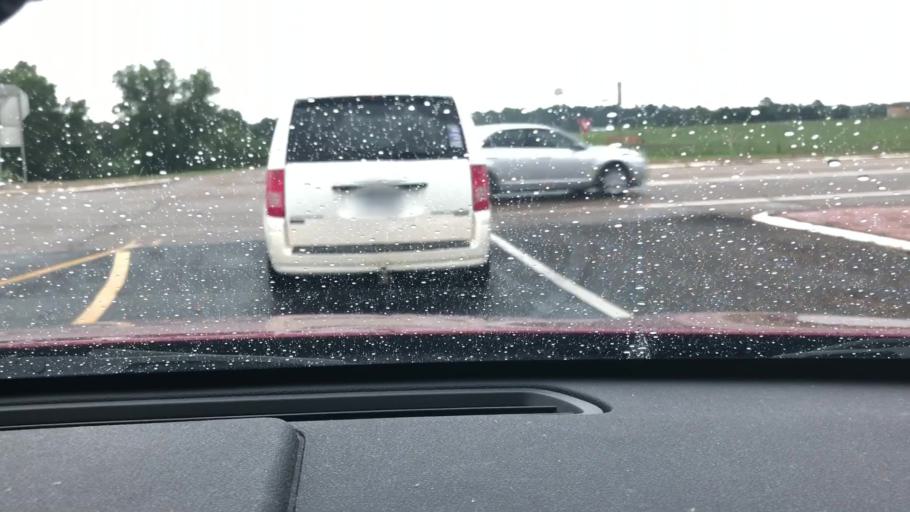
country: US
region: Arkansas
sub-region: Columbia County
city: Magnolia
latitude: 33.2972
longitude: -93.2361
